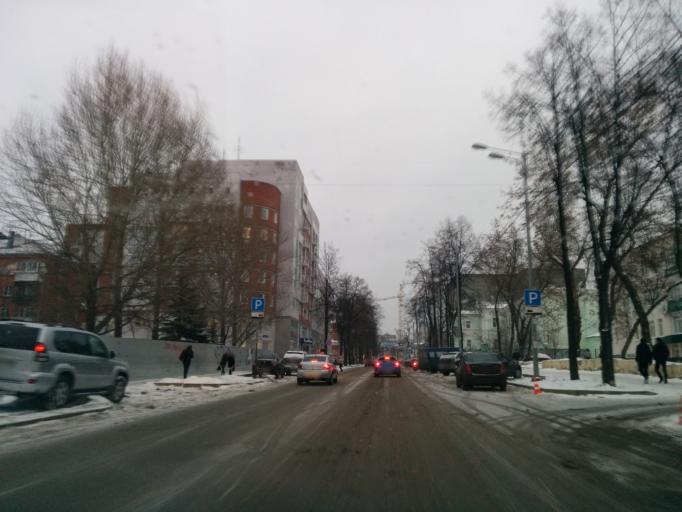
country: RU
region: Perm
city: Perm
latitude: 58.0058
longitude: 56.2327
